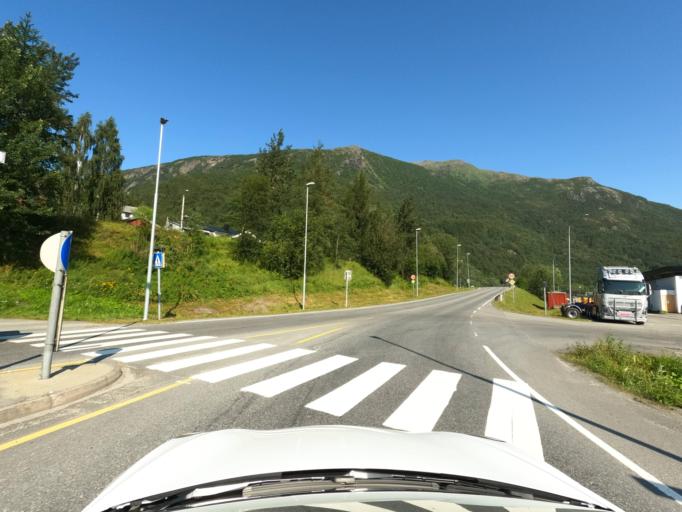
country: NO
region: Nordland
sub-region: Narvik
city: Narvik
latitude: 68.4119
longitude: 17.4312
